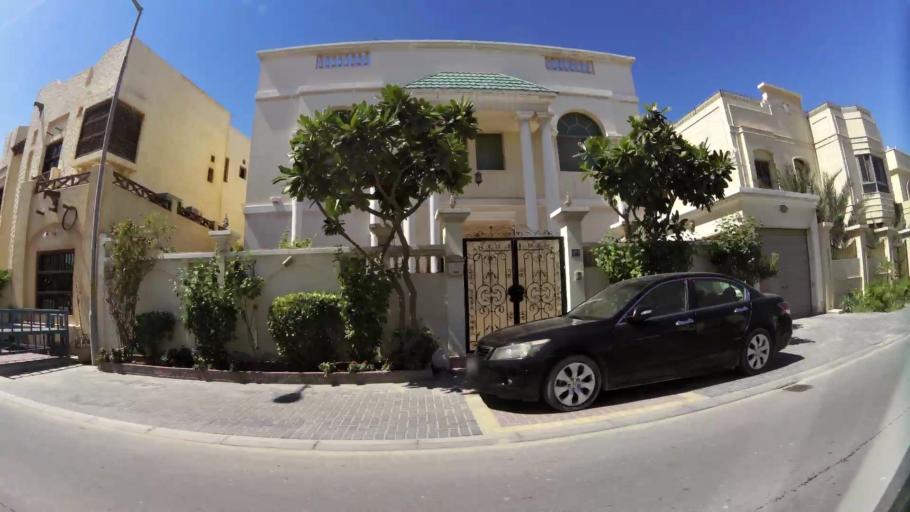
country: BH
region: Muharraq
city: Al Muharraq
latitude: 26.2737
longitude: 50.6053
